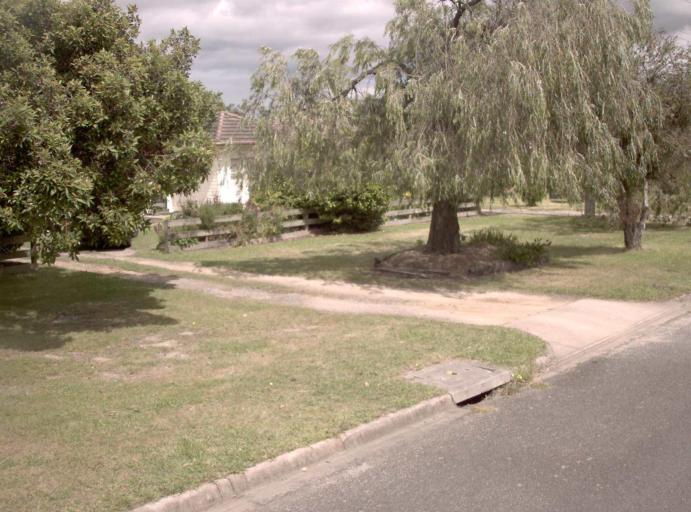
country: AU
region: Victoria
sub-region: Latrobe
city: Moe
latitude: -38.0724
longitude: 146.1785
